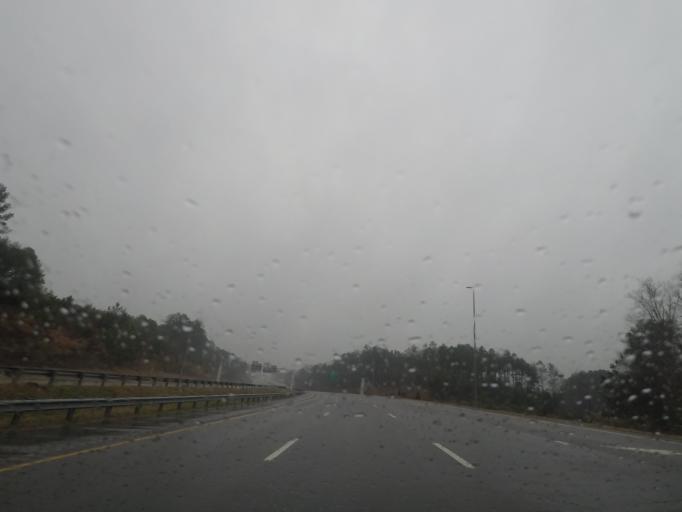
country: US
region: North Carolina
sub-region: Wake County
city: Morrisville
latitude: 35.8964
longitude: -78.8762
